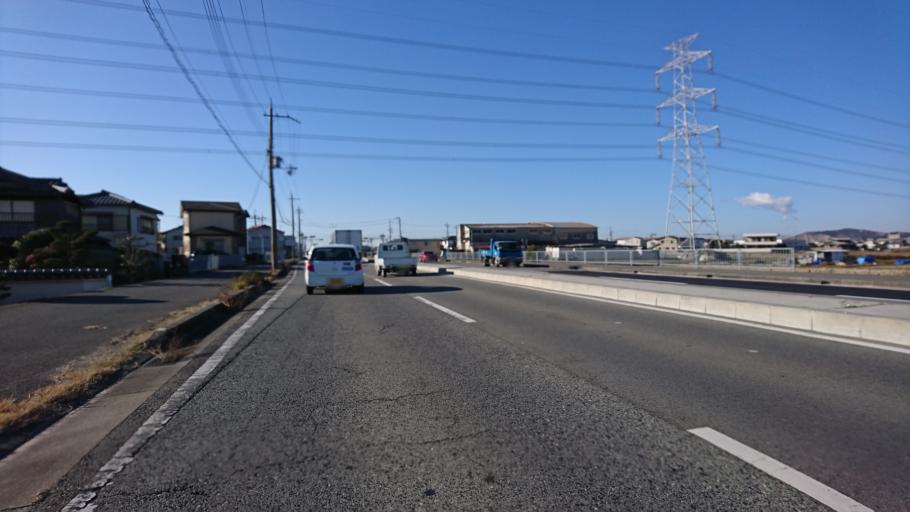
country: JP
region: Hyogo
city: Kakogawacho-honmachi
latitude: 34.7988
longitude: 134.8290
